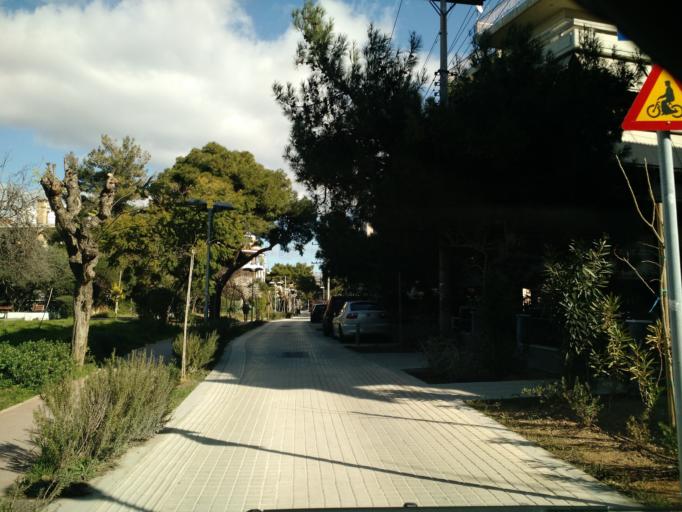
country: GR
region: Attica
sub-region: Nomarchia Athinas
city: Agia Paraskevi
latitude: 38.0177
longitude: 23.8231
